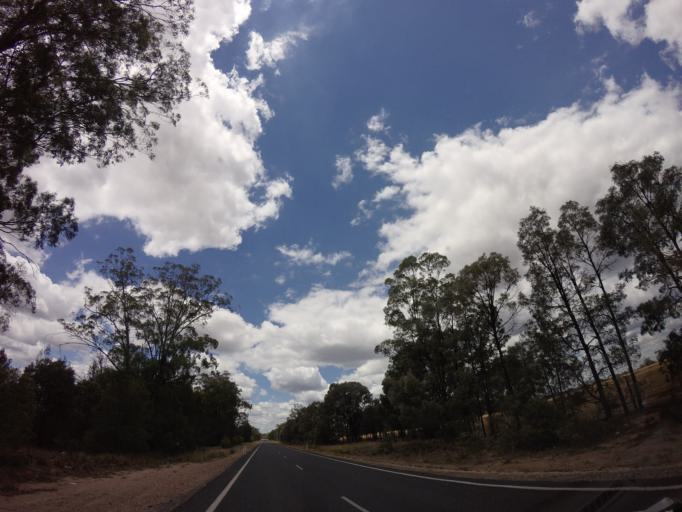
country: AU
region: Queensland
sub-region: Goondiwindi
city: Goondiwindi
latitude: -28.0130
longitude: 150.8710
